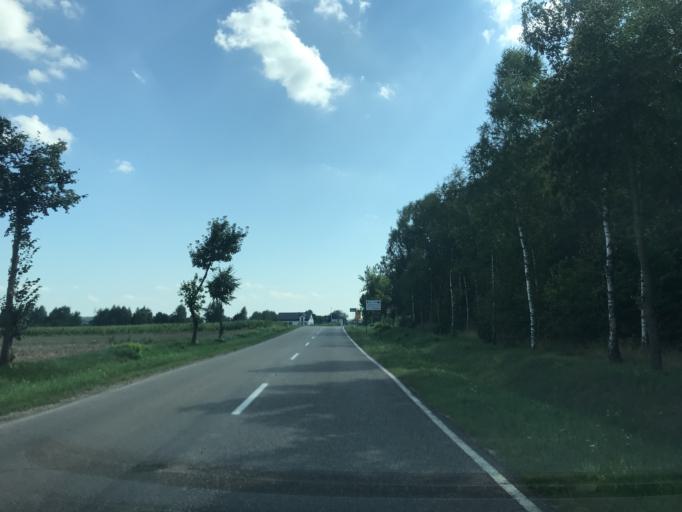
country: PL
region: Masovian Voivodeship
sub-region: Powiat zurominski
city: Lubowidz
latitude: 53.1816
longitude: 19.8499
